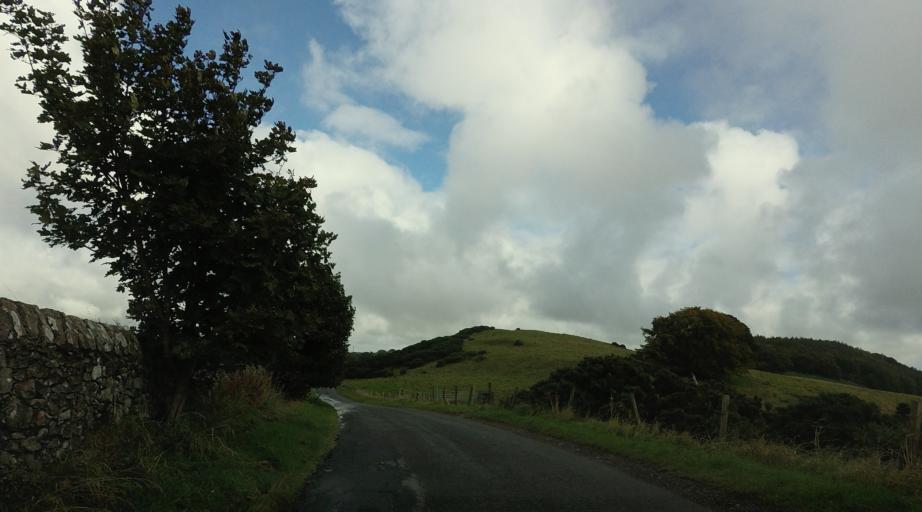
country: GB
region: Scotland
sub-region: Fife
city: Balmullo
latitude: 56.3663
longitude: -2.9717
